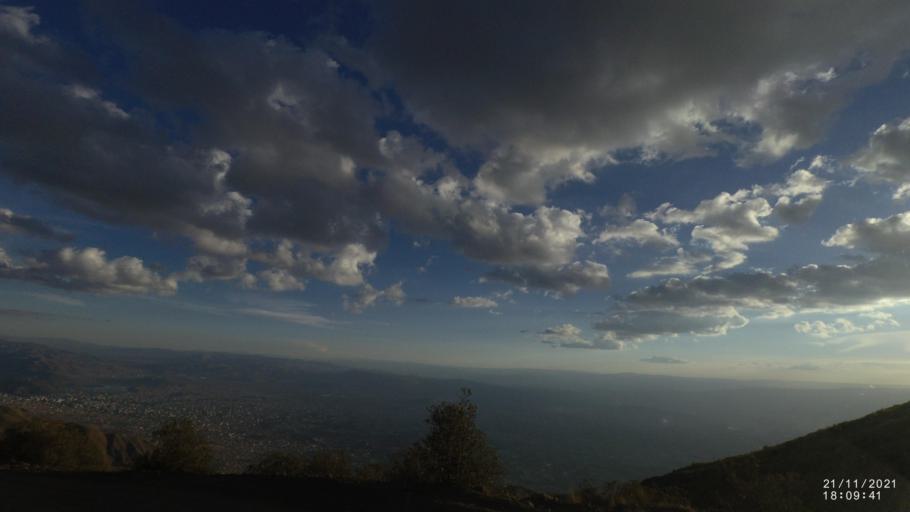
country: BO
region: Cochabamba
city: Cochabamba
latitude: -17.2841
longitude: -66.2129
